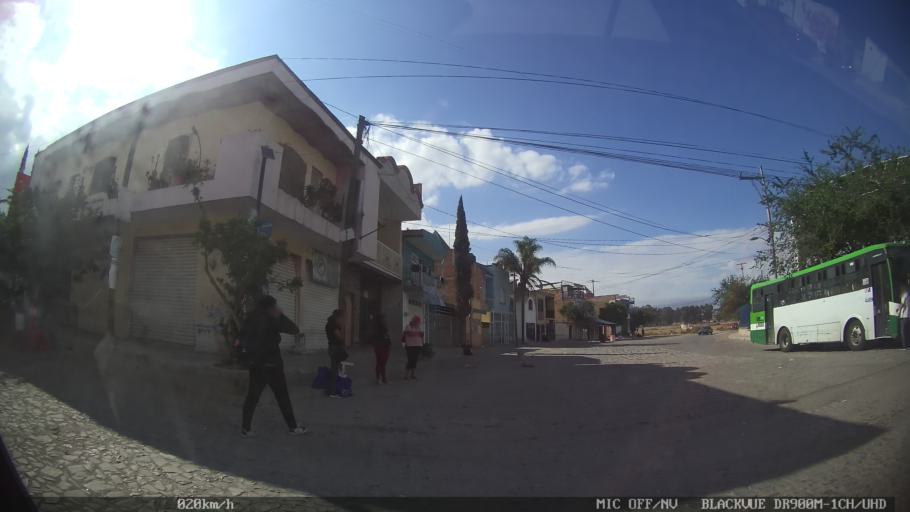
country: MX
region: Jalisco
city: Tonala
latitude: 20.6541
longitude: -103.2475
